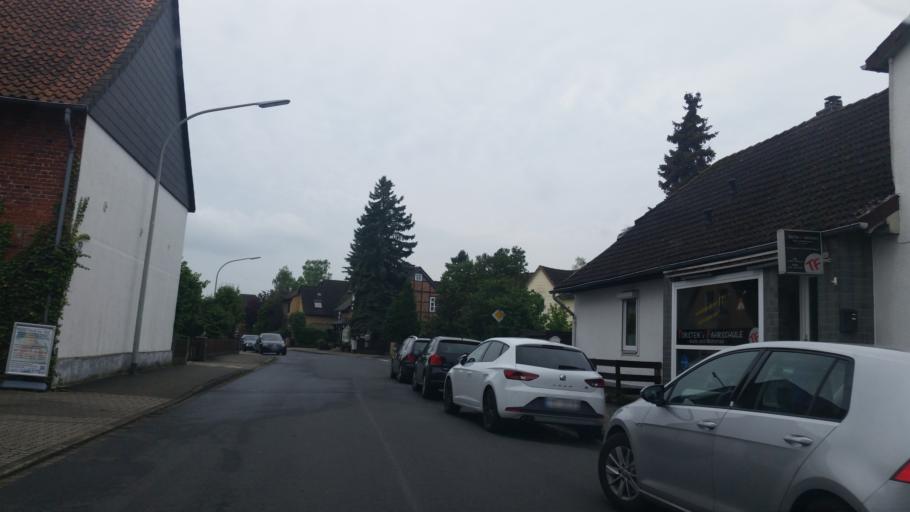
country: DE
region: Lower Saxony
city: Vordorf
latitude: 52.3241
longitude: 10.5589
